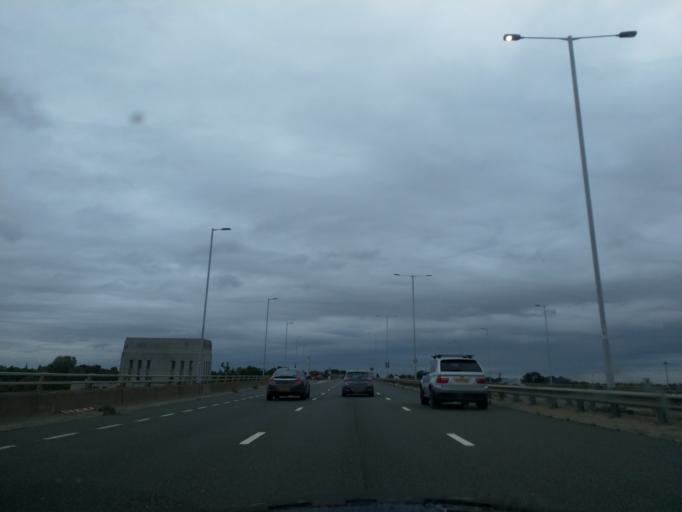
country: GB
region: England
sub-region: Greater London
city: Feltham
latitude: 51.4267
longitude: -0.4054
